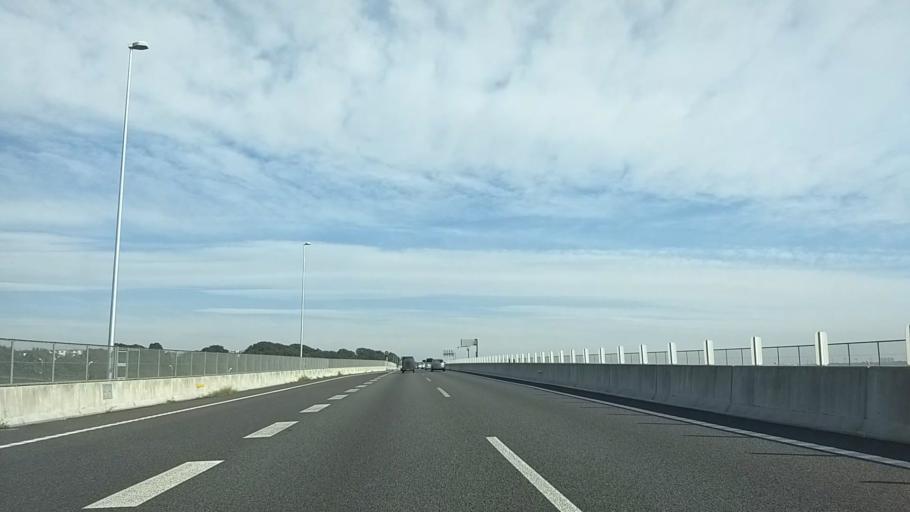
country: JP
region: Kanagawa
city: Zama
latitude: 35.4833
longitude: 139.3716
